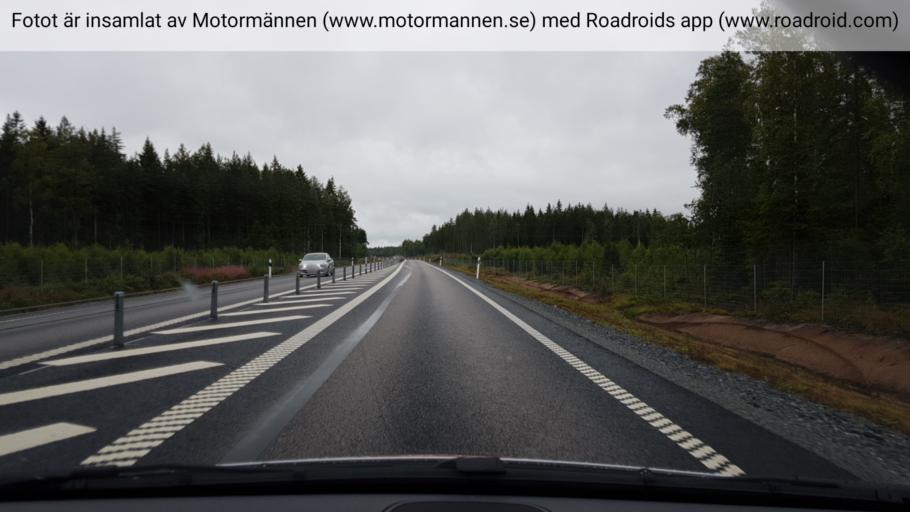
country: SE
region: Uppsala
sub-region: Heby Kommun
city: Tarnsjo
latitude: 60.0745
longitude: 16.9112
